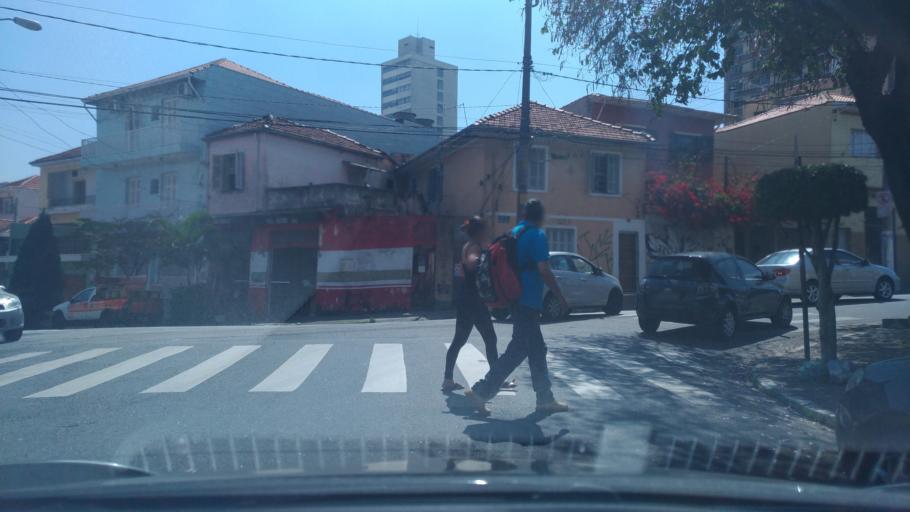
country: BR
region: Sao Paulo
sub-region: Sao Paulo
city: Sao Paulo
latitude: -23.5690
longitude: -46.5897
